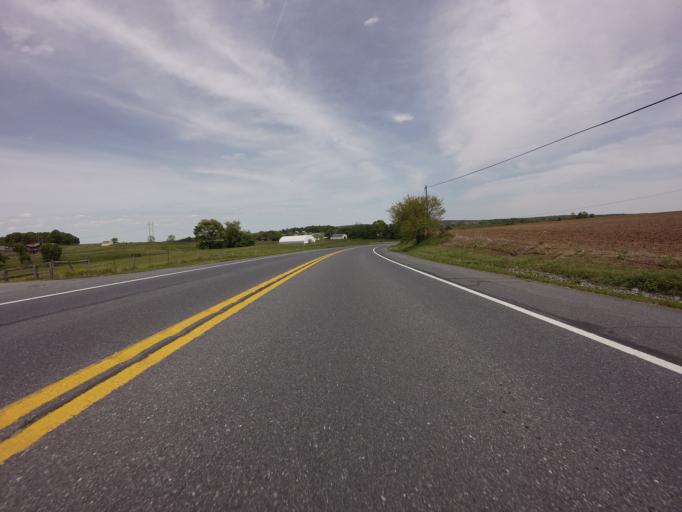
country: US
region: Maryland
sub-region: Frederick County
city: Linganore
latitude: 39.5007
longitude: -77.2003
